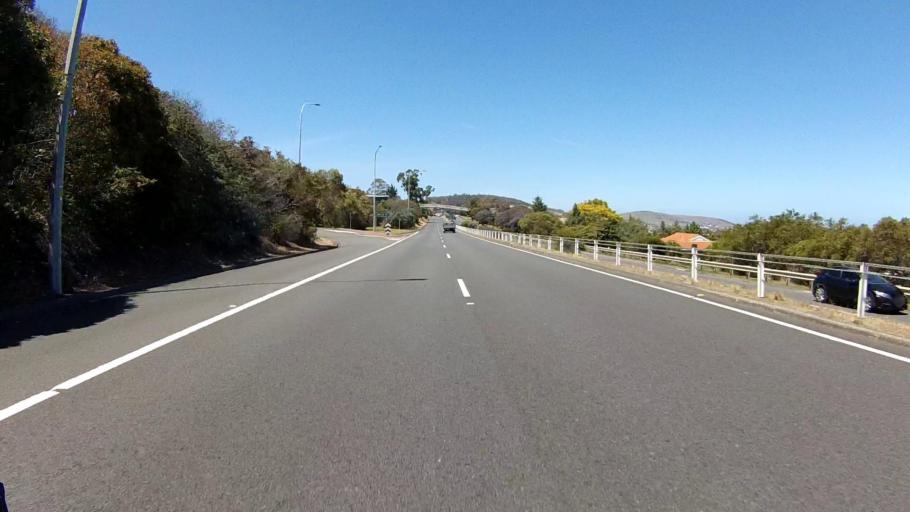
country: AU
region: Tasmania
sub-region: Clarence
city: Howrah
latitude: -42.8738
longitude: 147.4021
